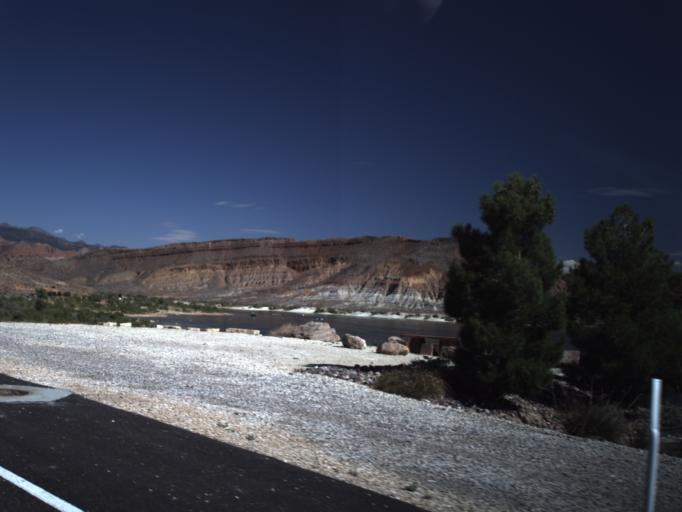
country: US
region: Utah
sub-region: Washington County
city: Hurricane
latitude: 37.1794
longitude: -113.3960
